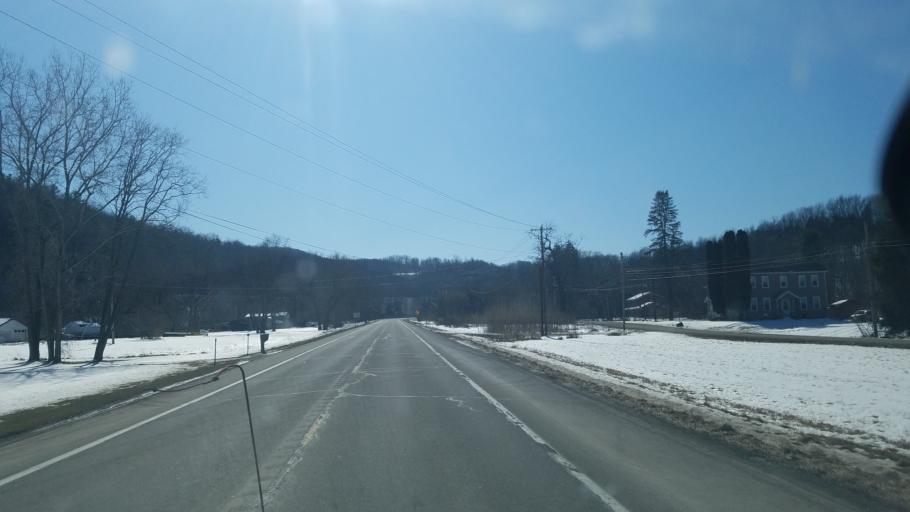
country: US
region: New York
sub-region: Allegany County
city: Alfred
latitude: 42.2843
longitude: -77.7492
